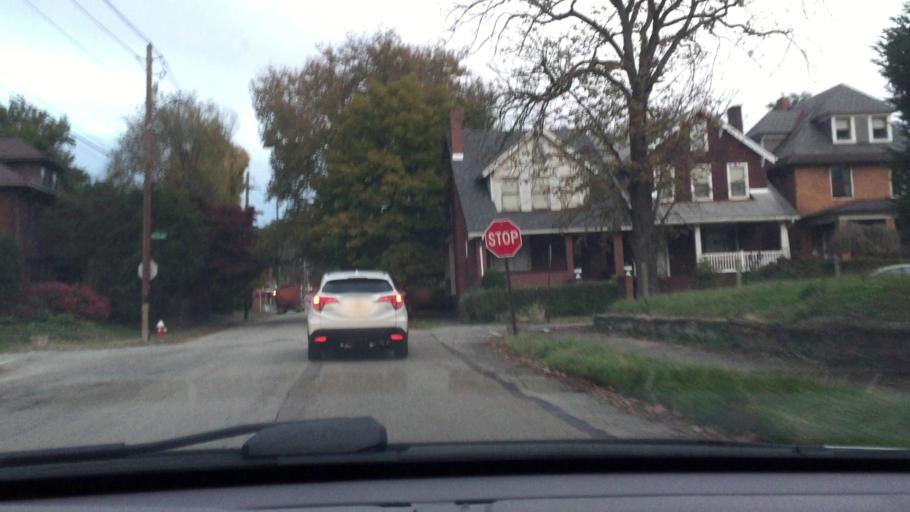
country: US
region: Pennsylvania
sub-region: Westmoreland County
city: Lower Burrell
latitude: 40.5567
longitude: -79.7634
